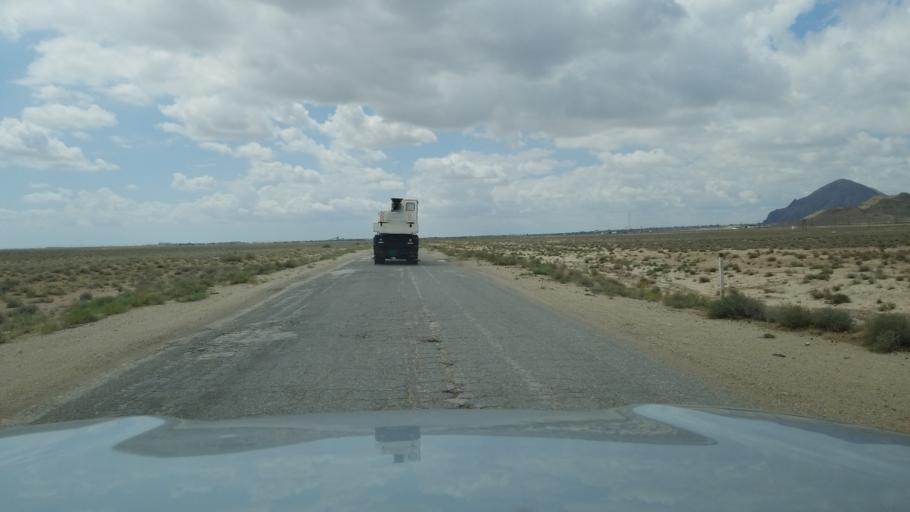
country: TM
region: Balkan
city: Balkanabat
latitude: 39.4834
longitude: 54.4364
